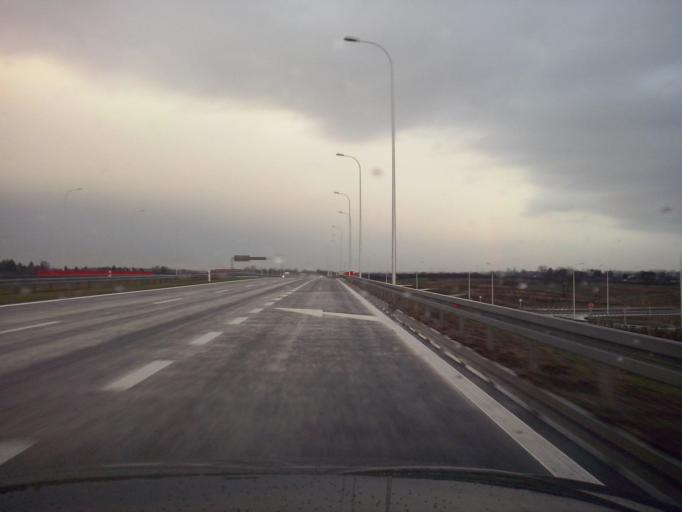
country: PL
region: Lublin Voivodeship
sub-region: Powiat lubelski
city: Jastkow
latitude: 51.2809
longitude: 22.4611
